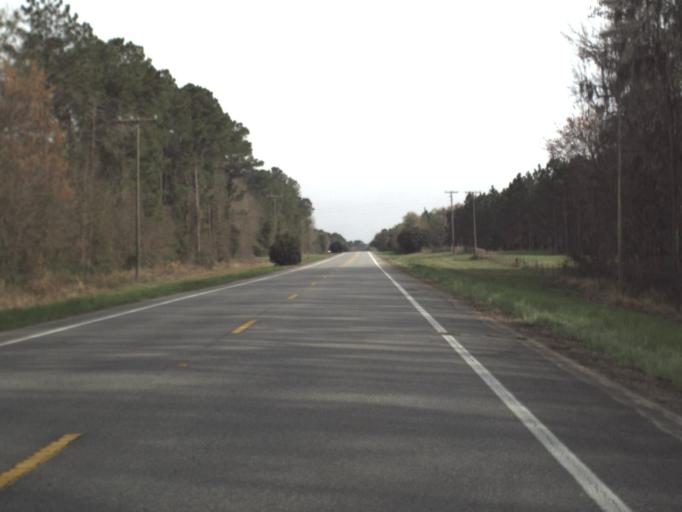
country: US
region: Florida
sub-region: Jefferson County
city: Monticello
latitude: 30.5181
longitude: -83.7837
